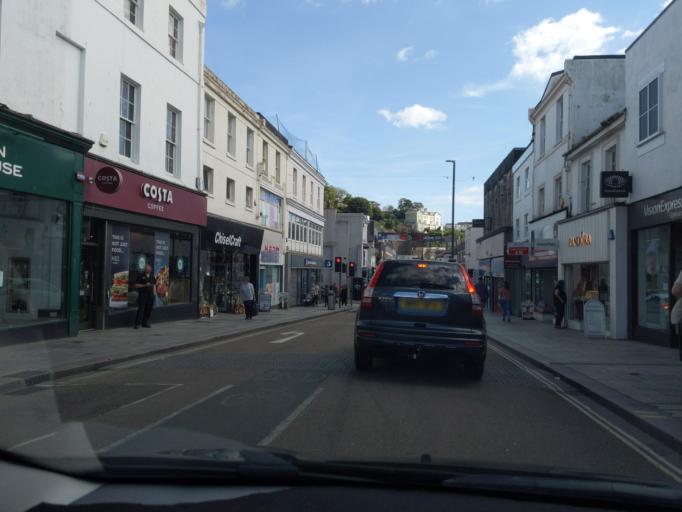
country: GB
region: England
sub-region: Borough of Torbay
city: Torquay
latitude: 50.4667
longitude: -3.5297
